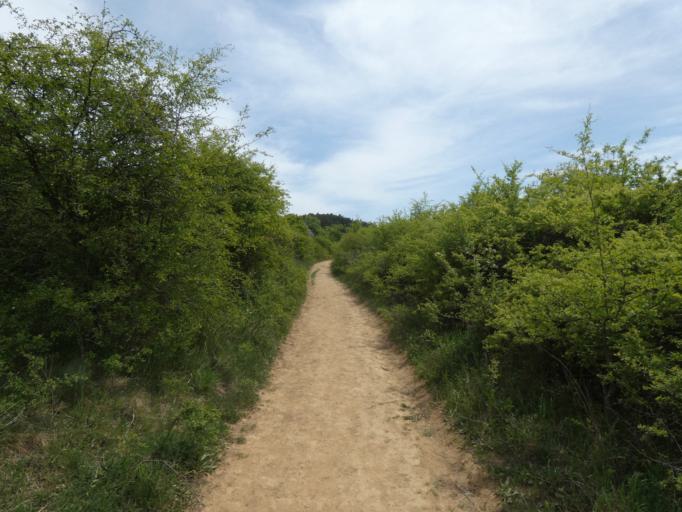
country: HU
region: Pest
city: Pilisborosjeno
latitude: 47.6155
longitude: 18.9749
